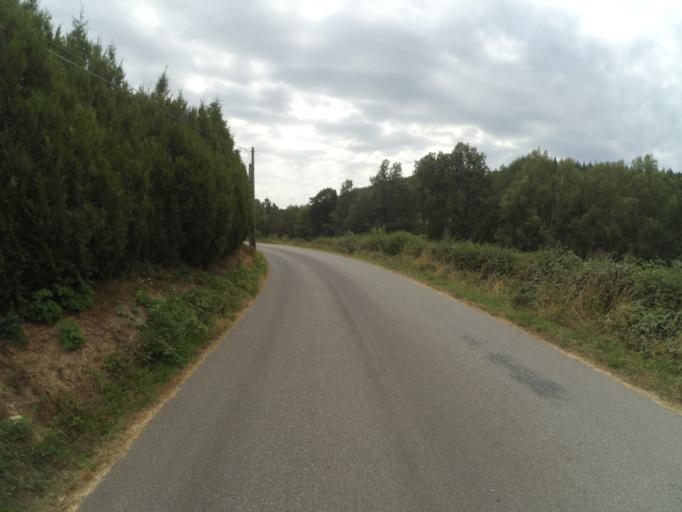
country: FR
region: Limousin
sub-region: Departement de la Creuse
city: La Courtine
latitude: 45.6659
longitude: 2.1651
